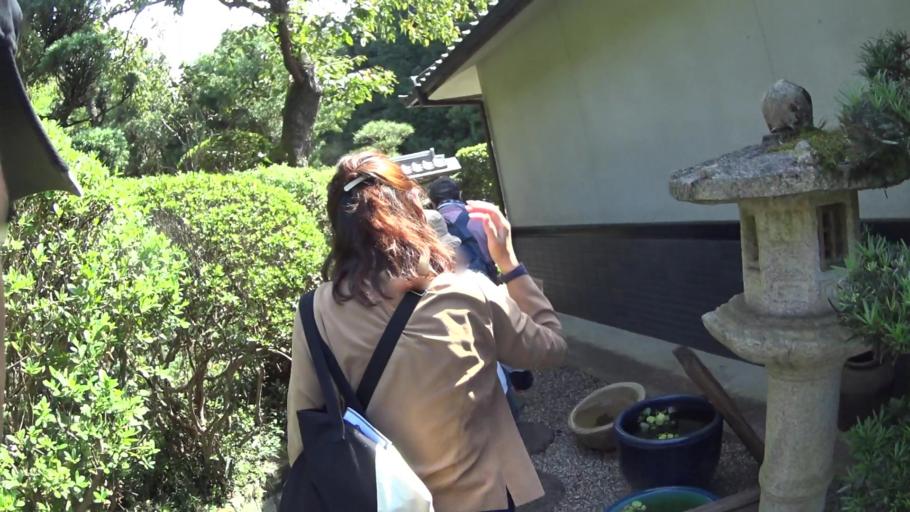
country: JP
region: Nara
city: Sakurai
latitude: 34.5324
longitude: 135.8517
